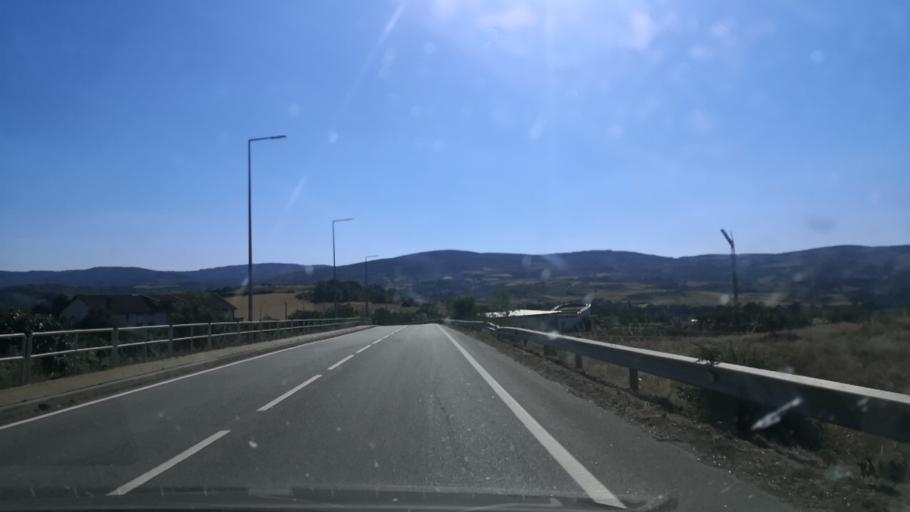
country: PT
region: Braganca
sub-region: Braganca Municipality
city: Braganca
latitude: 41.7785
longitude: -6.7816
